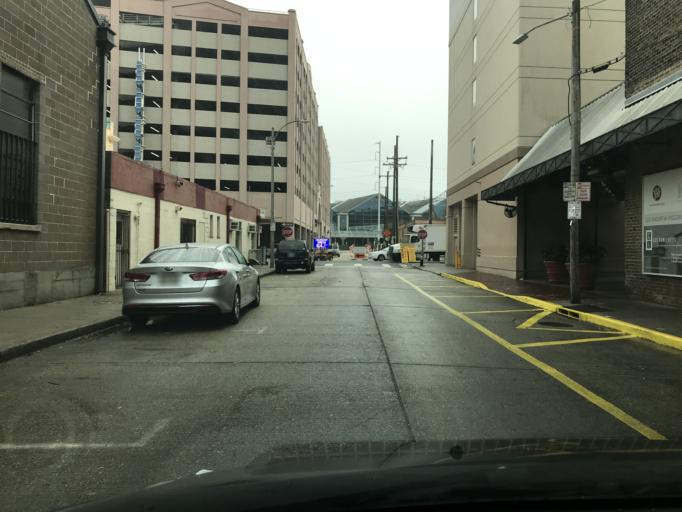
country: US
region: Louisiana
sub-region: Orleans Parish
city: New Orleans
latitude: 29.9420
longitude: -90.0663
